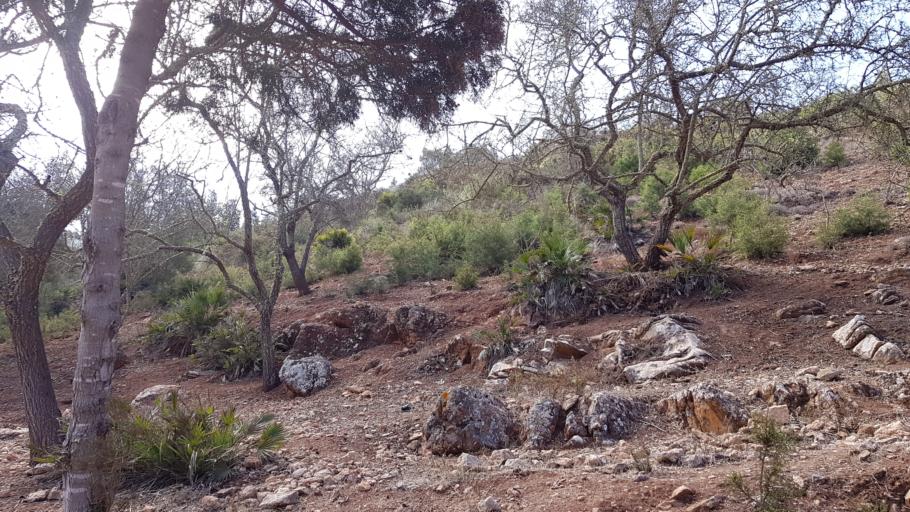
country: MA
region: Taza-Al Hoceima-Taounate
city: Tirhanimine
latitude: 35.2034
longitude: -4.0166
